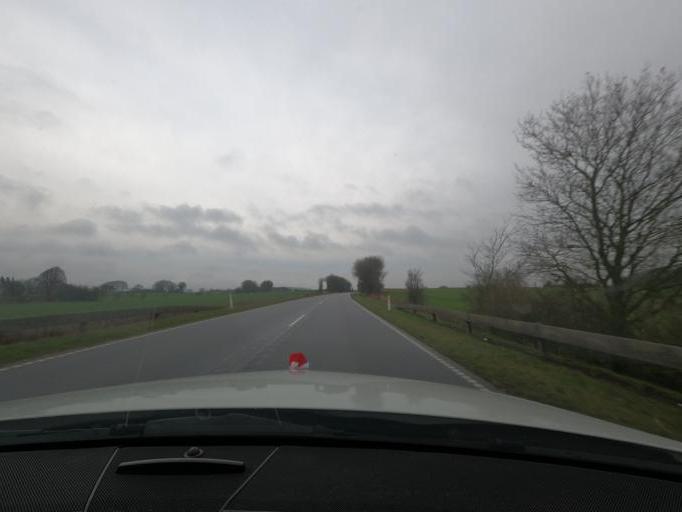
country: DK
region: South Denmark
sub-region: Haderslev Kommune
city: Haderslev
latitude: 55.1957
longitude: 9.4206
